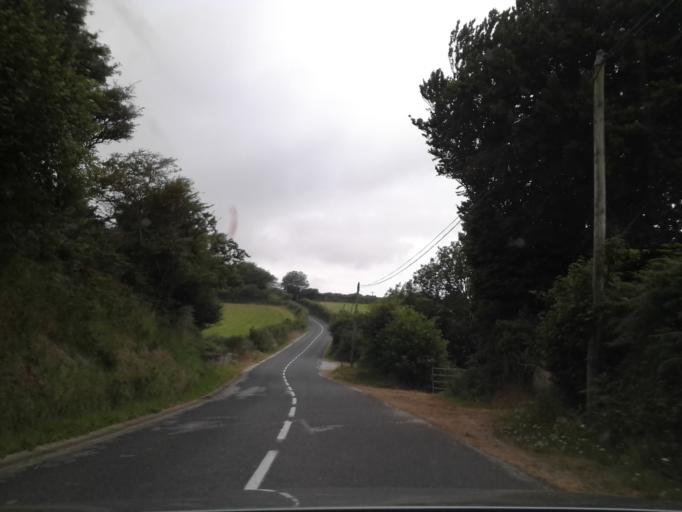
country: FR
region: Lower Normandy
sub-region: Departement de la Manche
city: Beaumont-Hague
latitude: 49.6817
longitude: -1.8525
